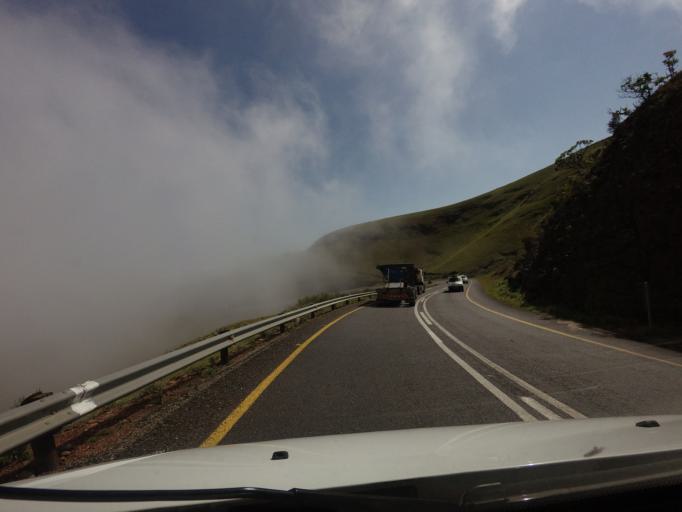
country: ZA
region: Mpumalanga
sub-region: Ehlanzeni District
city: Lydenburg
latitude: -25.1598
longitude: 30.6293
